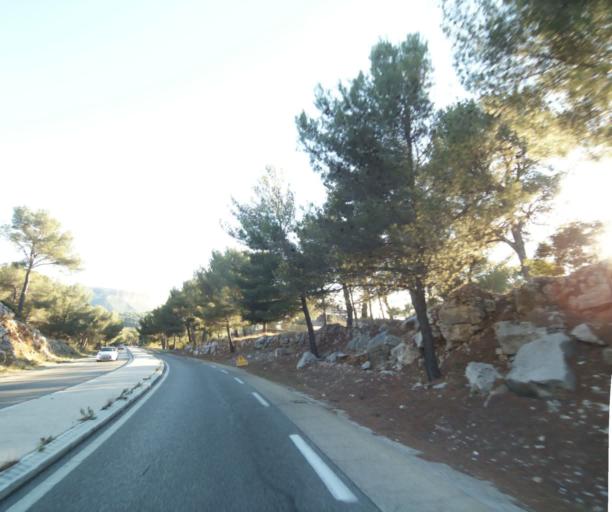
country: FR
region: Provence-Alpes-Cote d'Azur
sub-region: Departement des Bouches-du-Rhone
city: Cassis
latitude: 43.2352
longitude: 5.5432
